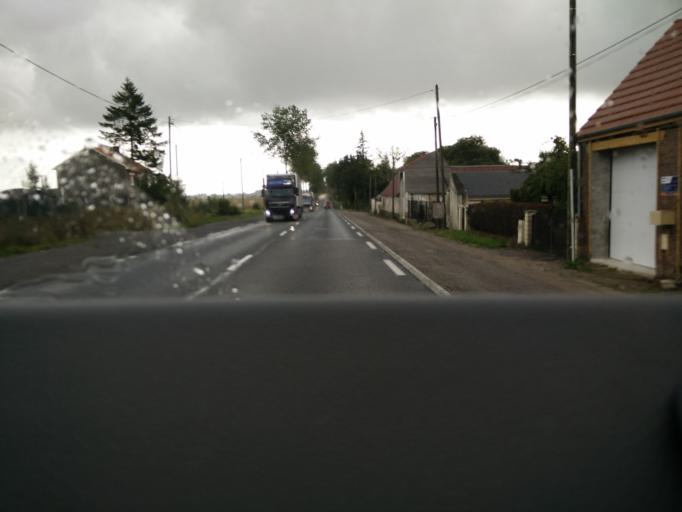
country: FR
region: Nord-Pas-de-Calais
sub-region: Departement du Pas-de-Calais
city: Savy-Berlette
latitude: 50.3504
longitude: 2.5259
